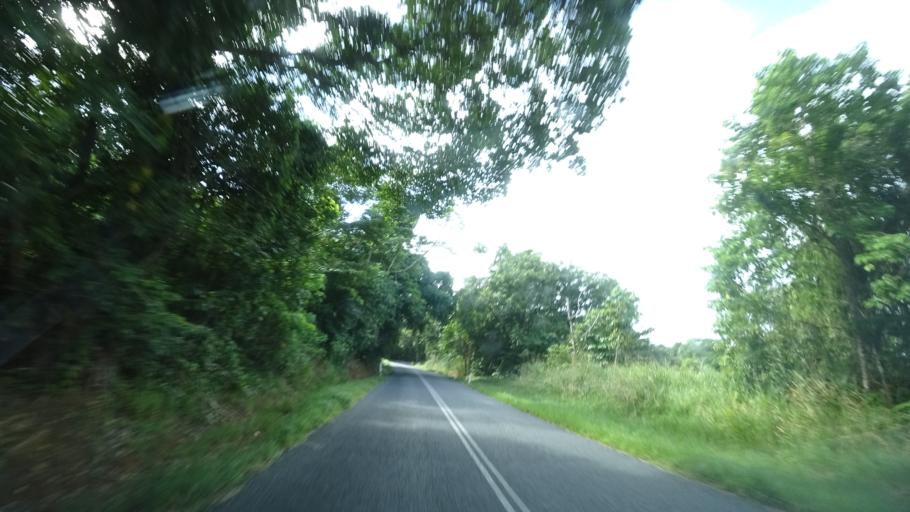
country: AU
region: Queensland
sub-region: Cairns
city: Port Douglas
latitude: -16.1037
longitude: 145.4578
